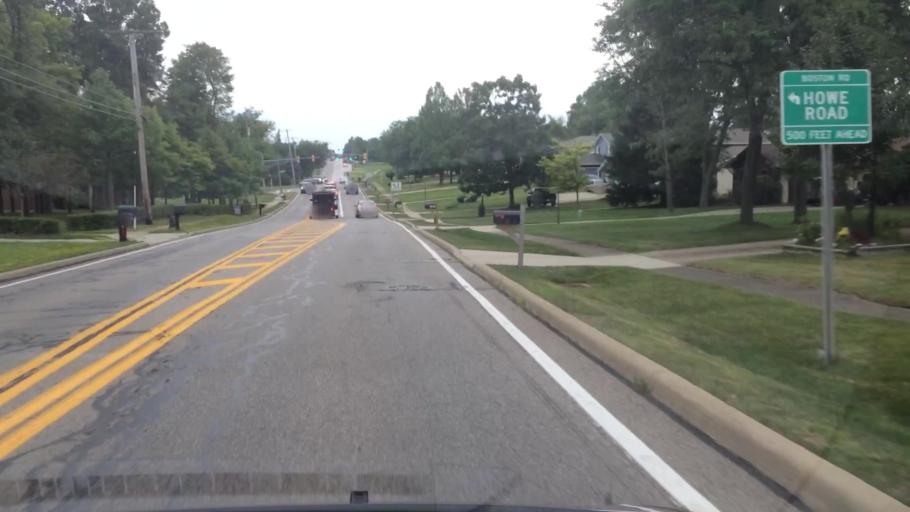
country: US
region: Ohio
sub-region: Cuyahoga County
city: Strongsville
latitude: 41.2760
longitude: -81.8128
